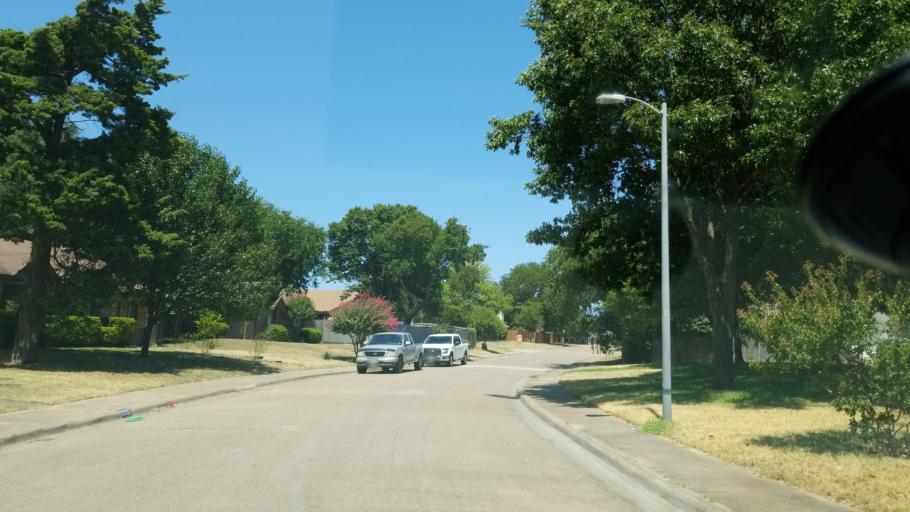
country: US
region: Texas
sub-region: Dallas County
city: Duncanville
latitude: 32.6358
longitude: -96.8871
